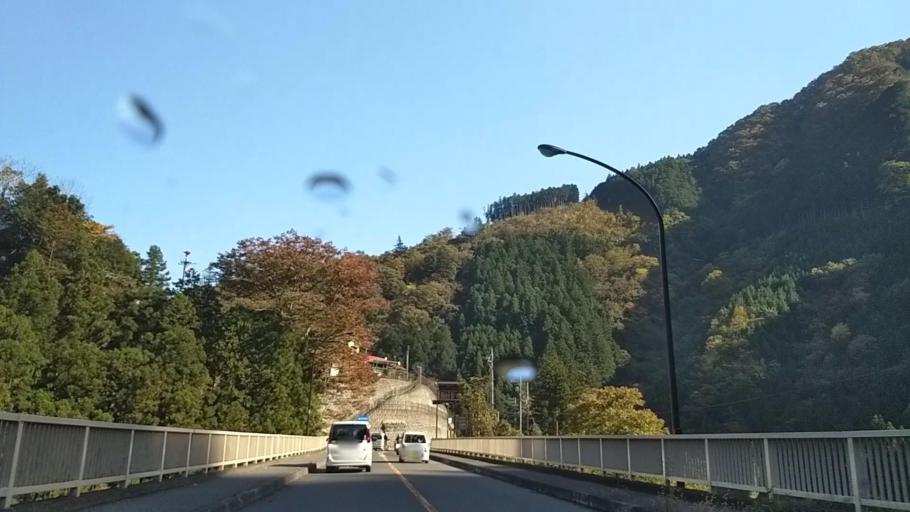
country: JP
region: Tokyo
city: Itsukaichi
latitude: 35.7993
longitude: 139.0823
